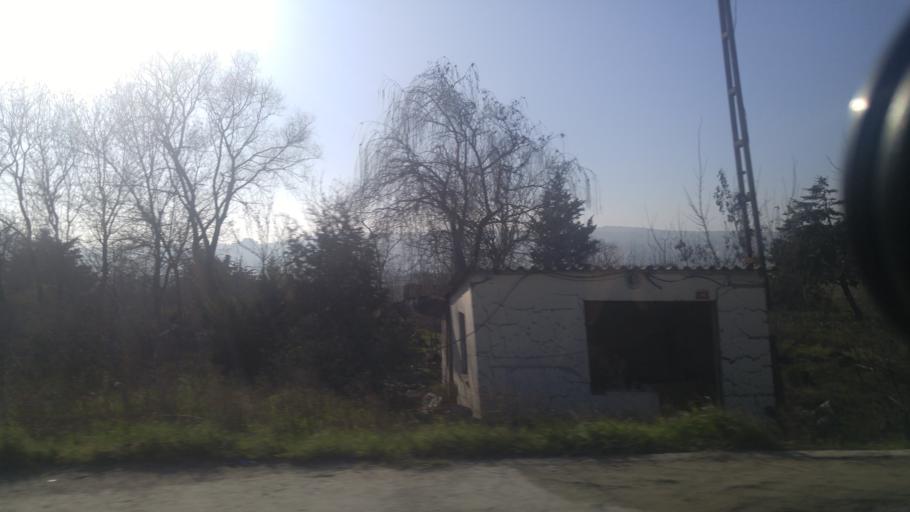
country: TR
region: Istanbul
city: Muratbey
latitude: 41.0918
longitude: 28.5133
